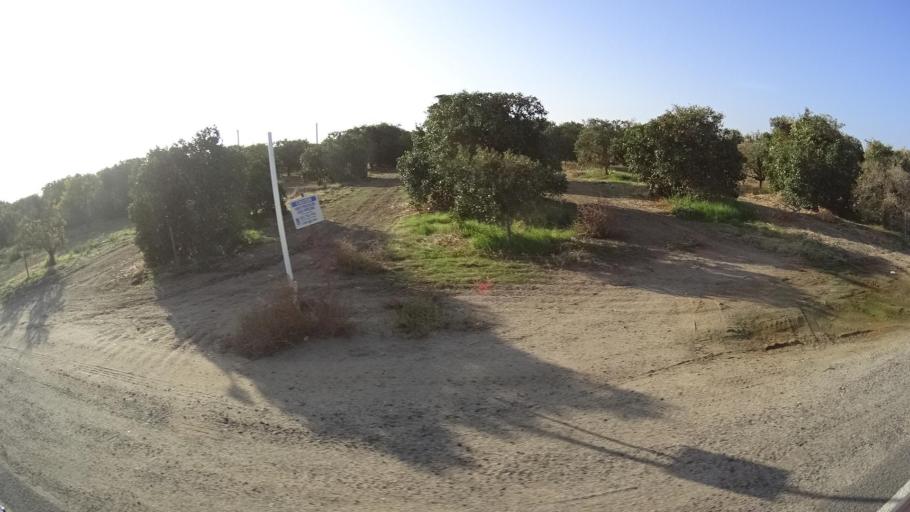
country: US
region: California
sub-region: Tulare County
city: Richgrove
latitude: 35.7620
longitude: -119.0577
